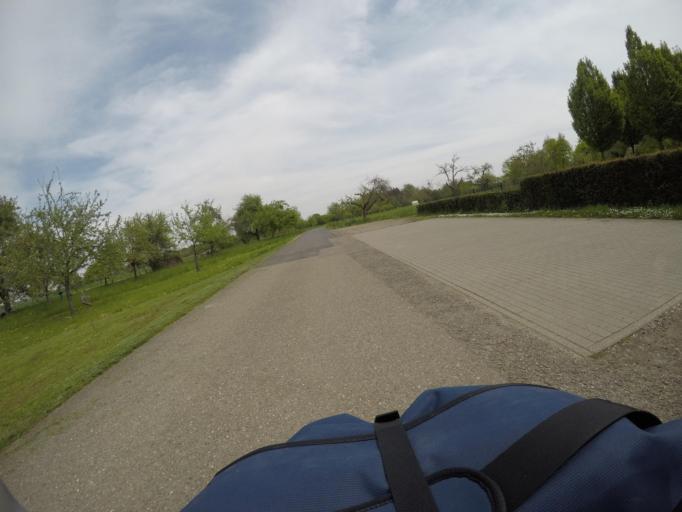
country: DE
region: Baden-Wuerttemberg
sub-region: Freiburg Region
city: Kehl
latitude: 48.6078
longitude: 7.8429
